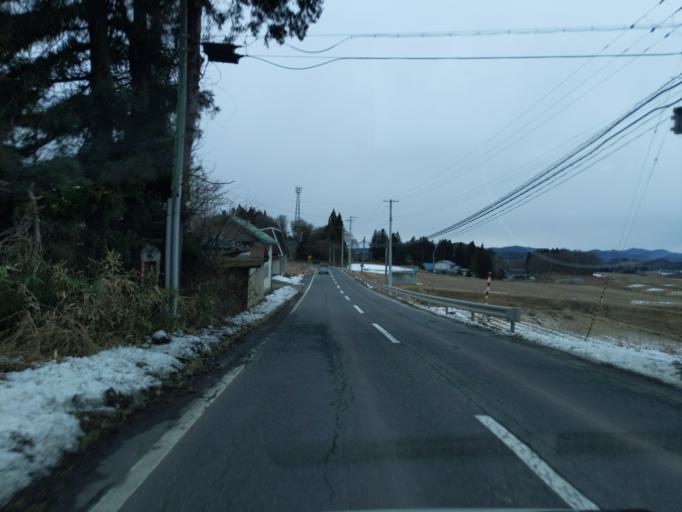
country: JP
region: Iwate
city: Mizusawa
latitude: 39.1816
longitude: 141.2574
